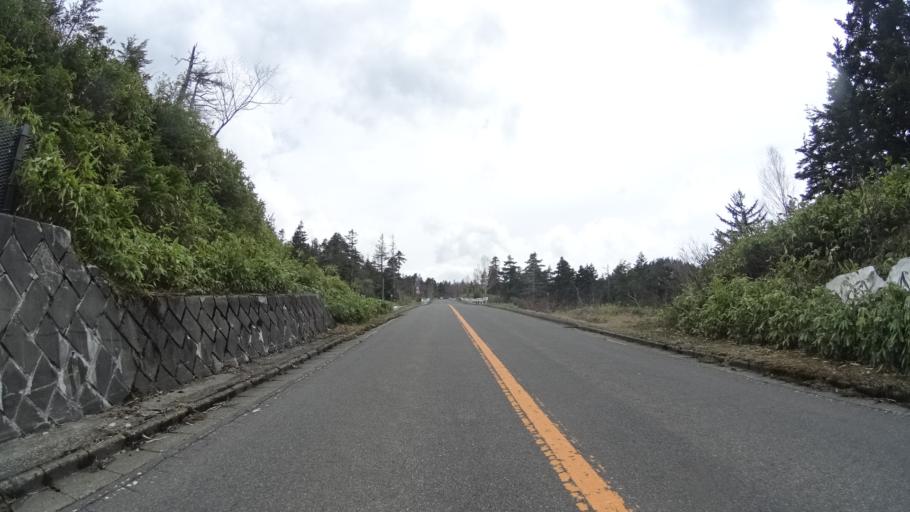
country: JP
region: Nagano
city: Nakano
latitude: 36.6733
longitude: 138.5134
